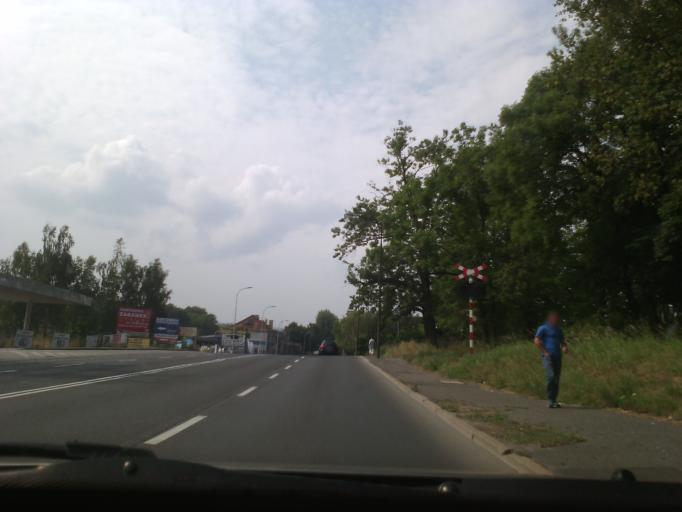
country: PL
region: Lower Silesian Voivodeship
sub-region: Powiat walbrzyski
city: Walbrzych
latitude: 50.7799
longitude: 16.2801
